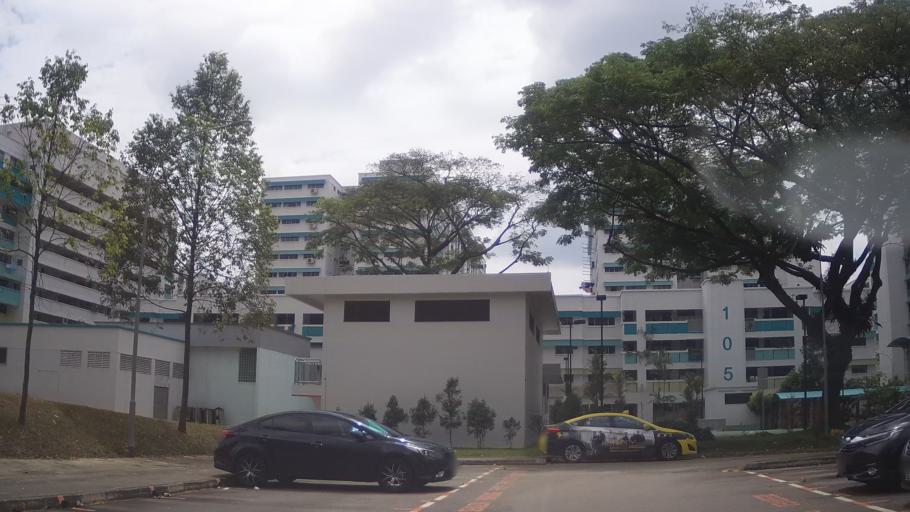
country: MY
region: Johor
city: Johor Bahru
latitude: 1.3786
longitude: 103.7671
